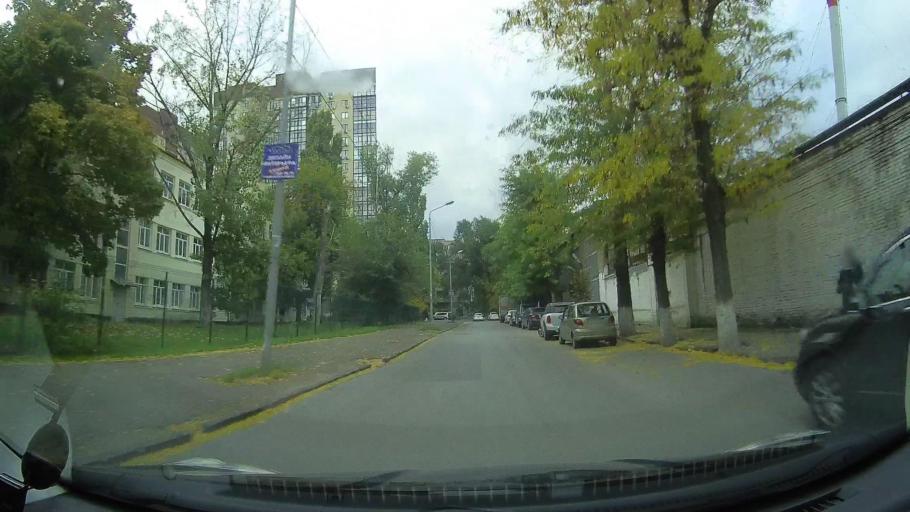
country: RU
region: Rostov
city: Rostov-na-Donu
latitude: 47.2342
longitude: 39.6983
